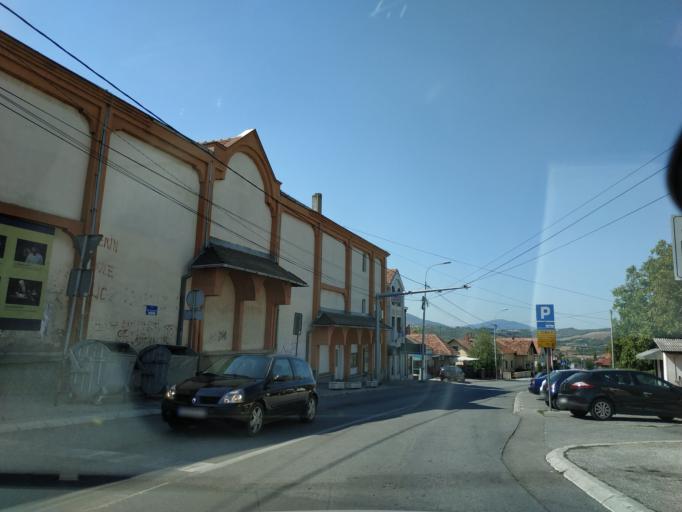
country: RS
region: Central Serbia
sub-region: Sumadijski Okrug
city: Topola
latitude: 44.2548
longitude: 20.6781
